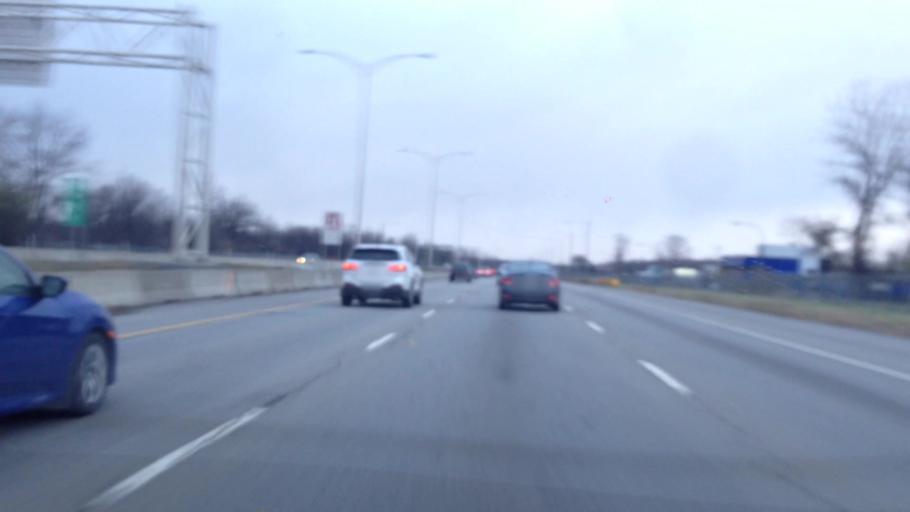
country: CA
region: Quebec
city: Baie-D'Urfe
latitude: 45.4293
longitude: -73.9130
